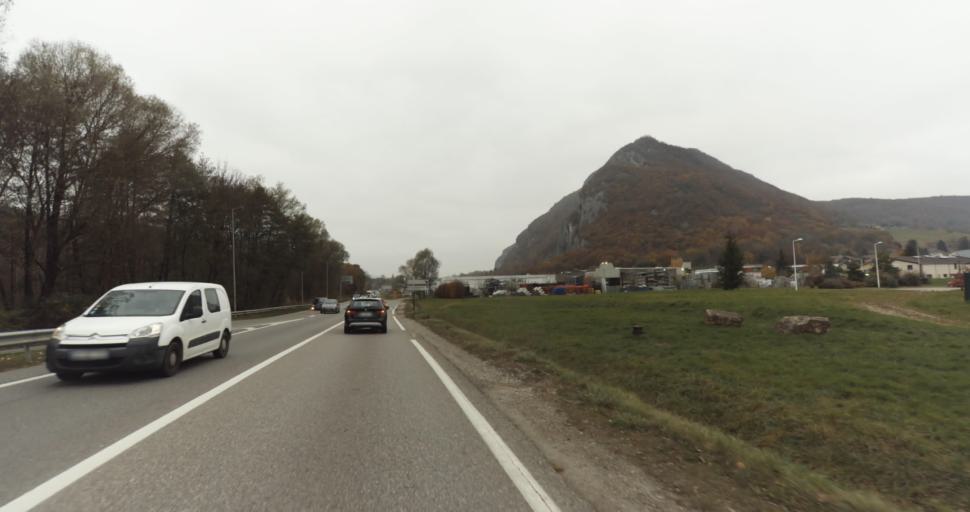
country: FR
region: Rhone-Alpes
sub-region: Departement de la Haute-Savoie
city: Poisy
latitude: 45.9394
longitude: 6.0677
